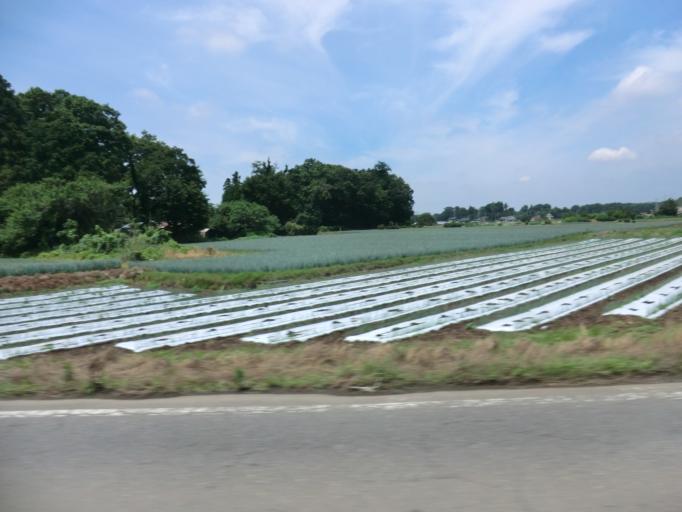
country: JP
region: Ibaraki
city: Iwai
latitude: 36.0814
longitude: 139.8958
